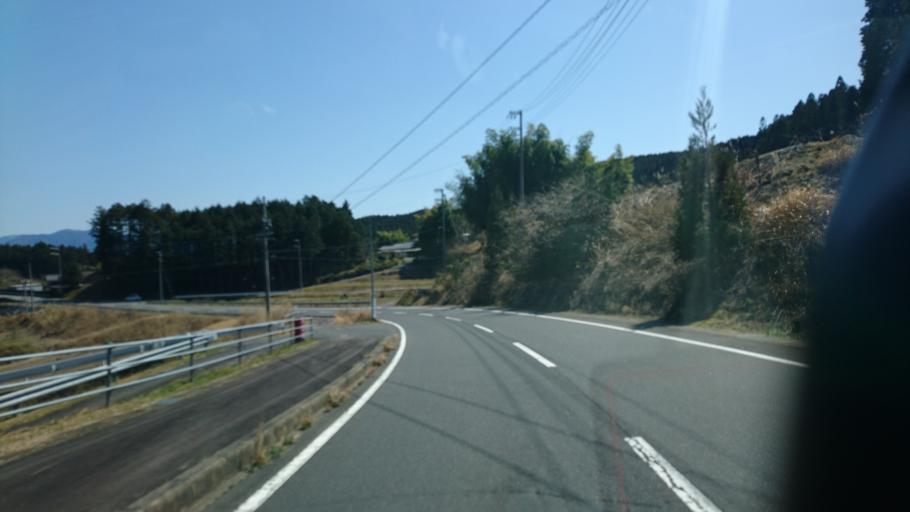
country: JP
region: Gifu
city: Mizunami
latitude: 35.4597
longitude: 137.3554
